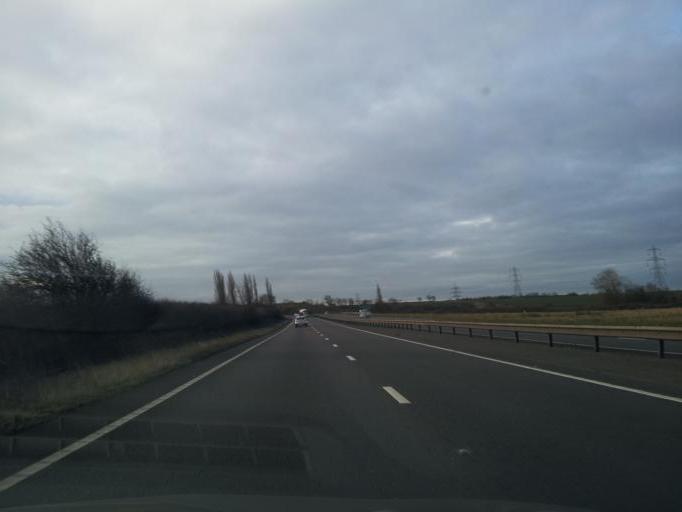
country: GB
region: England
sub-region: Lincolnshire
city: Long Bennington
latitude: 52.9976
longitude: -0.7633
